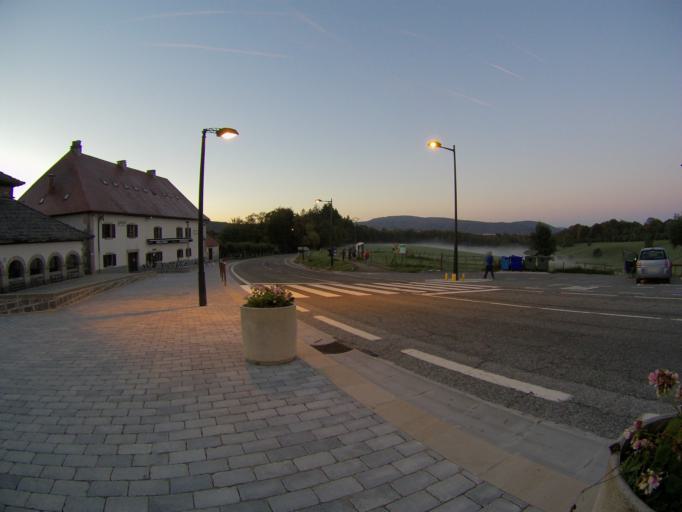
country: ES
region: Navarre
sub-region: Provincia de Navarra
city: Garralda
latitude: 43.0087
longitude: -1.3198
